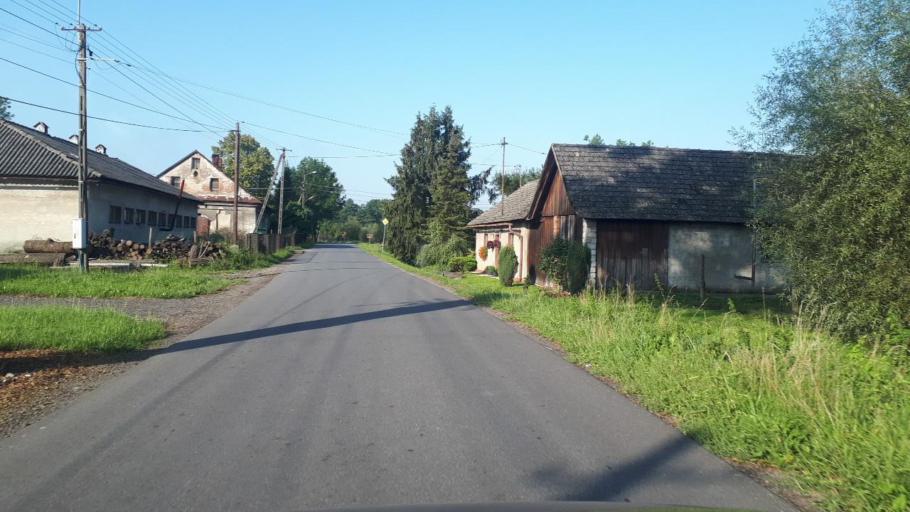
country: PL
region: Silesian Voivodeship
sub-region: Powiat cieszynski
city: Piersciec
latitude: 49.8599
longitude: 18.8526
